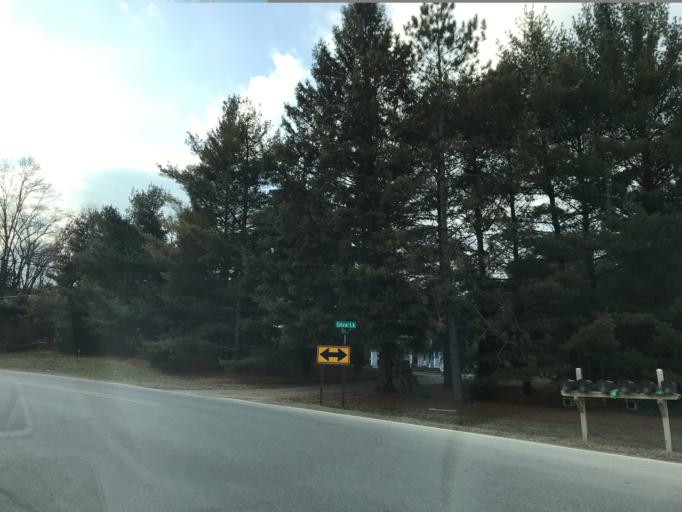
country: US
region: Michigan
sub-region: Livingston County
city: Whitmore Lake
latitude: 42.4715
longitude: -83.7260
